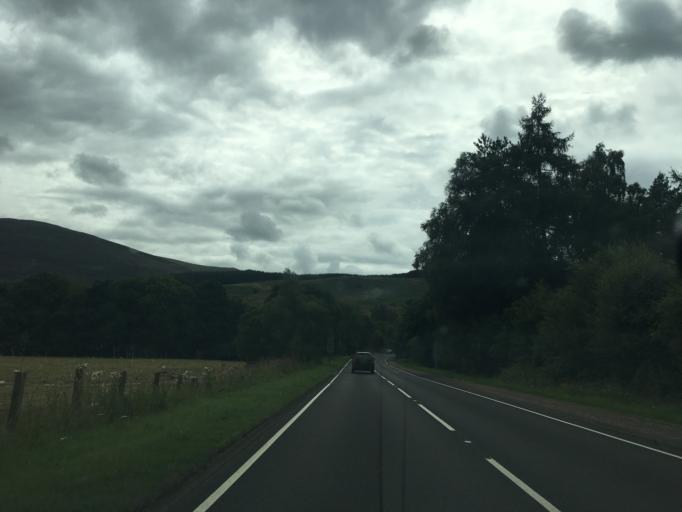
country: GB
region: Scotland
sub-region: Stirling
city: Callander
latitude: 56.3802
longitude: -4.2864
